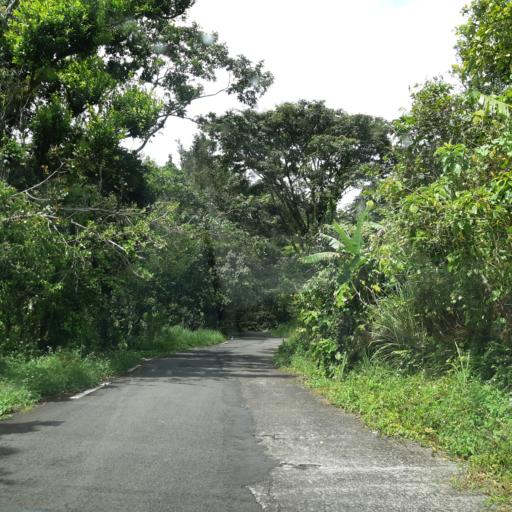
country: GP
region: Guadeloupe
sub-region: Guadeloupe
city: Saint-Claude
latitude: 16.0326
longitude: -61.6815
